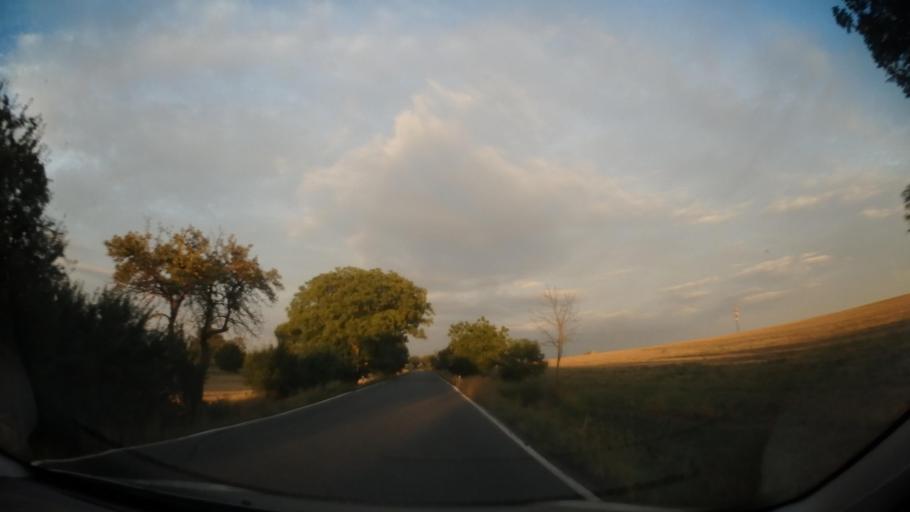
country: CZ
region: Central Bohemia
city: Loucen
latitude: 50.2381
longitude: 15.0068
